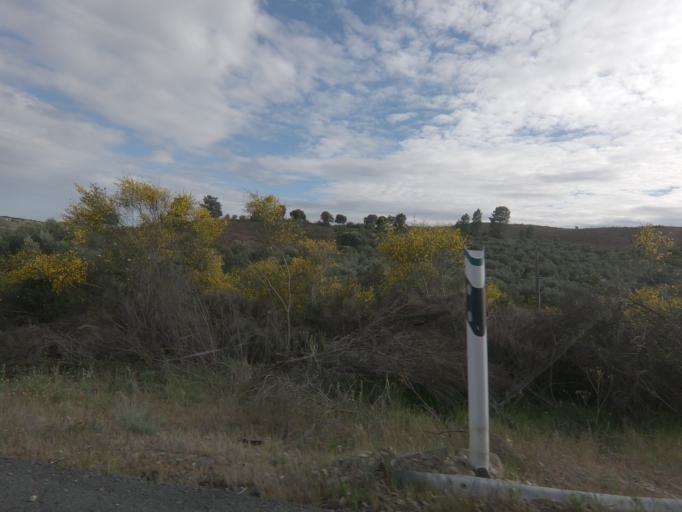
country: ES
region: Extremadura
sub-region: Provincia de Caceres
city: Perales del Puerto
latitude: 40.1243
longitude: -6.6764
